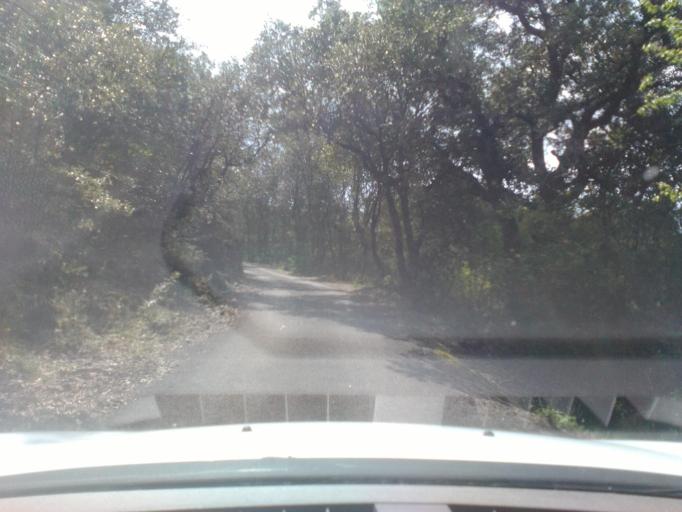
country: FR
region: Languedoc-Roussillon
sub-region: Departement du Gard
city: Saint-Hippolyte-du-Fort
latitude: 43.9914
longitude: 3.8652
